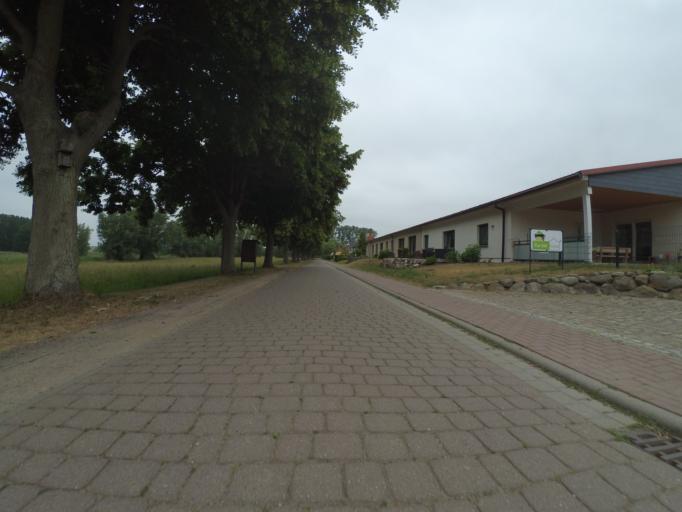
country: DE
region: Mecklenburg-Vorpommern
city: Goldberg
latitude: 53.5765
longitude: 12.0307
